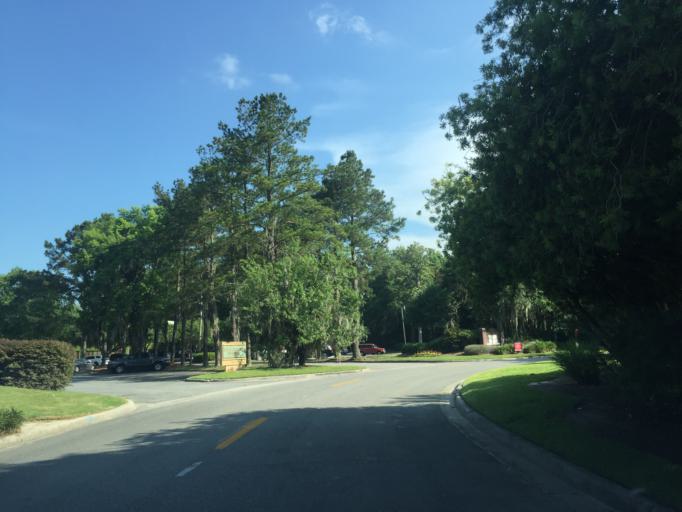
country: US
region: Georgia
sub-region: Chatham County
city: Isle of Hope
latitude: 32.0050
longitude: -81.1074
